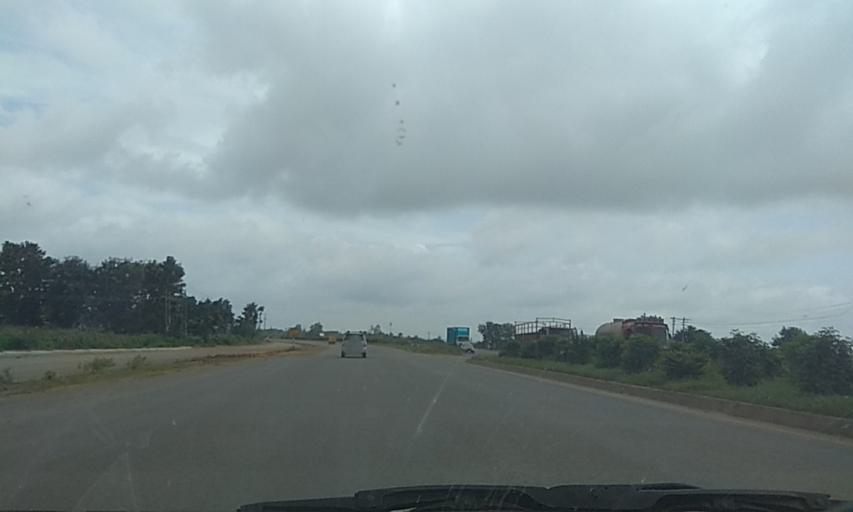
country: IN
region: Karnataka
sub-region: Dharwad
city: Kundgol
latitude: 15.1757
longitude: 75.1398
